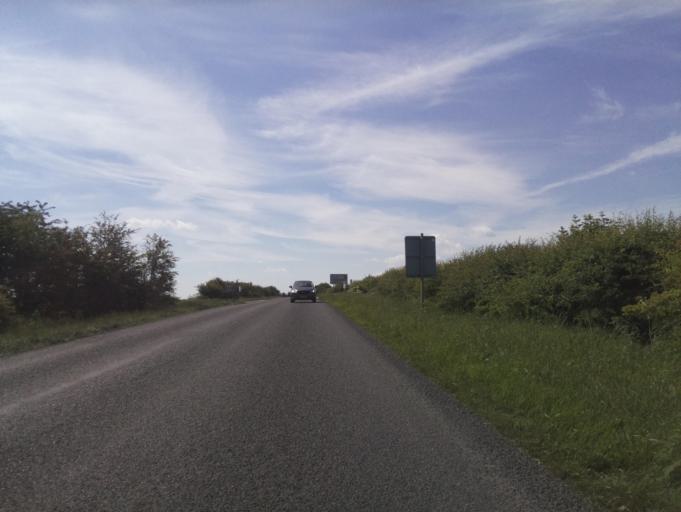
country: GB
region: England
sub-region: North Lincolnshire
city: Redbourne
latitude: 53.4222
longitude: -0.5495
